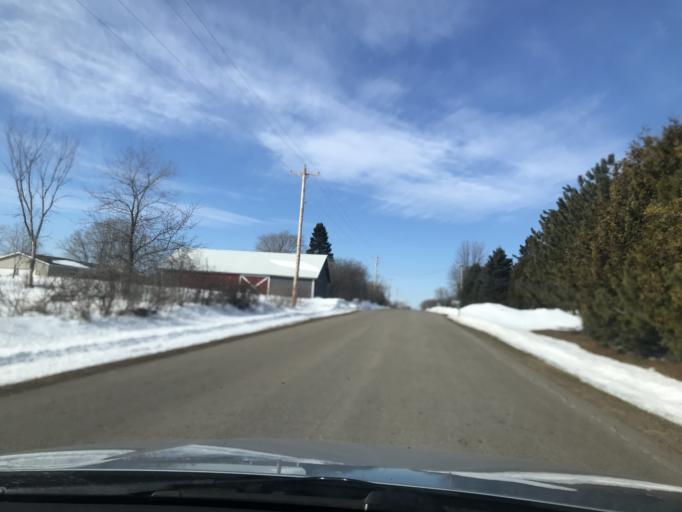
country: US
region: Wisconsin
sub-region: Oconto County
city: Gillett
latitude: 44.9692
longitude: -88.3134
